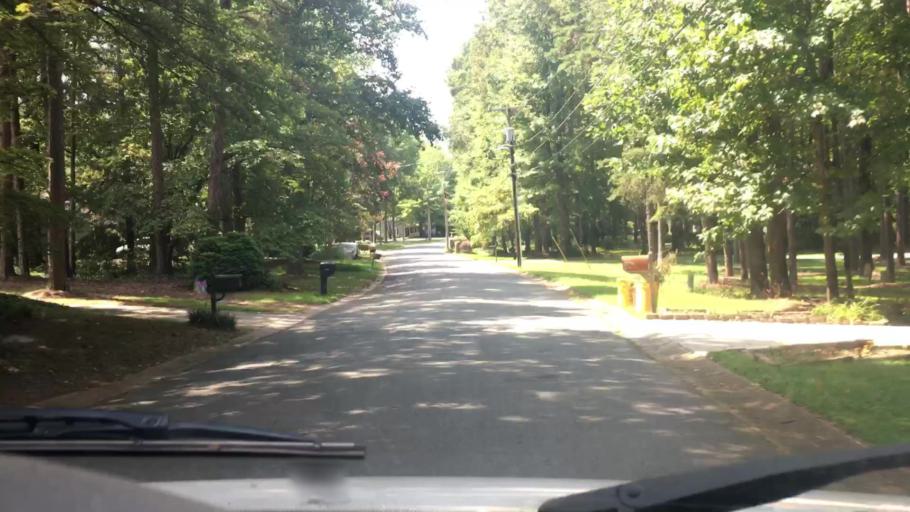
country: US
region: North Carolina
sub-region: Mecklenburg County
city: Cornelius
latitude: 35.4743
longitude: -80.8695
